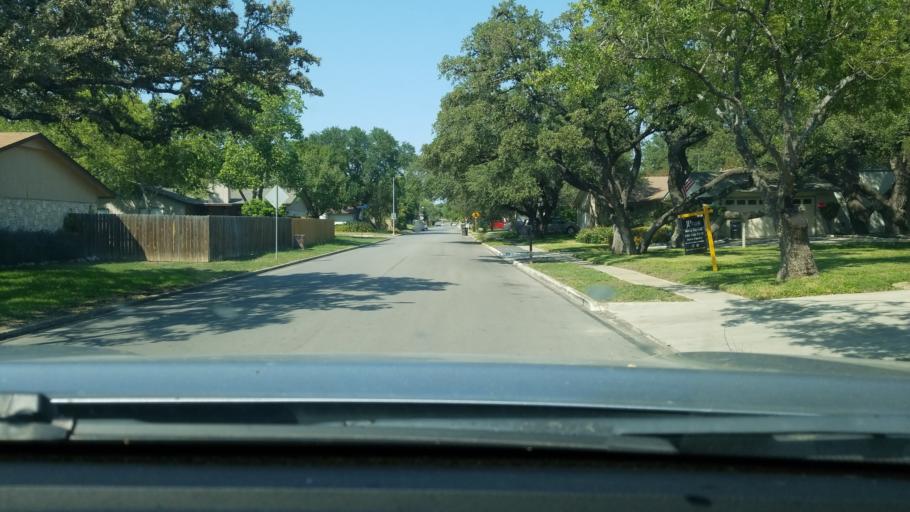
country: US
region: Texas
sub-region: Bexar County
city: Shavano Park
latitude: 29.5551
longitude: -98.6057
